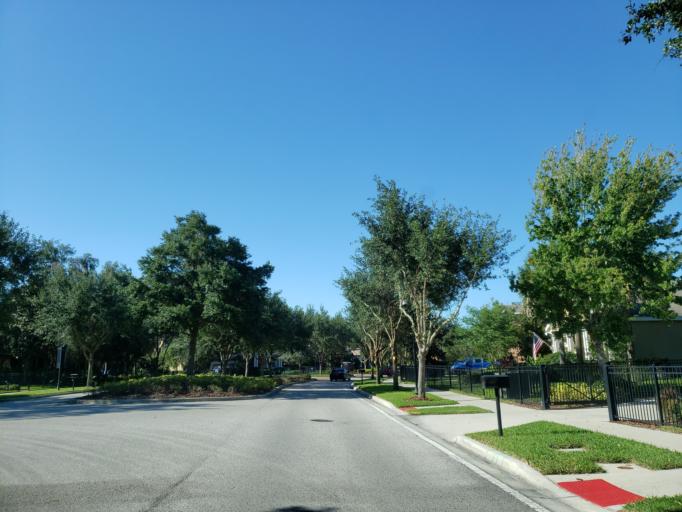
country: US
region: Florida
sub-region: Hillsborough County
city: Fish Hawk
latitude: 27.8463
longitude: -82.2140
